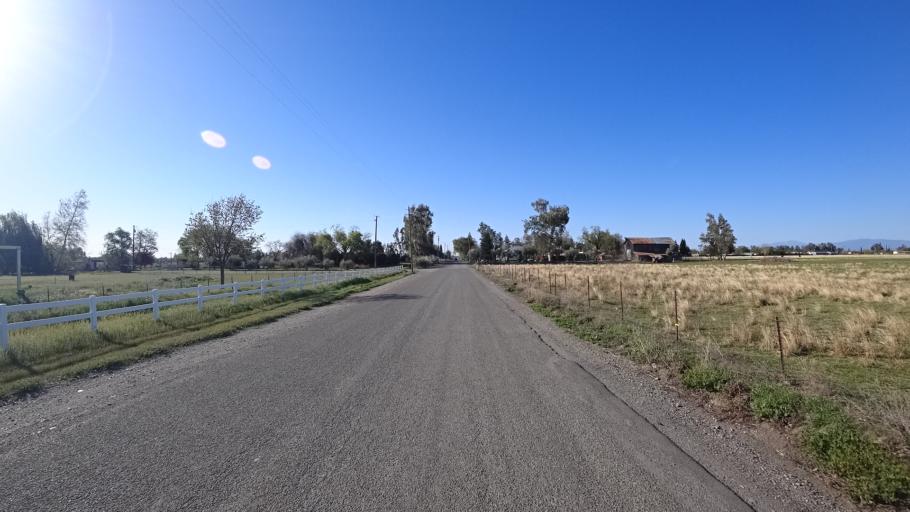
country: US
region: California
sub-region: Glenn County
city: Orland
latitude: 39.7637
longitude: -122.2202
